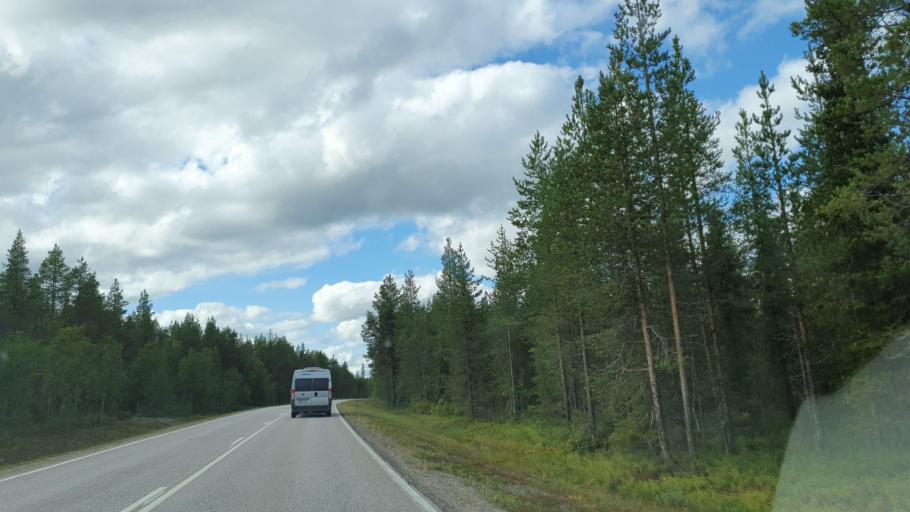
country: FI
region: Lapland
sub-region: Tunturi-Lappi
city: Muonio
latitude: 67.8599
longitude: 24.1383
